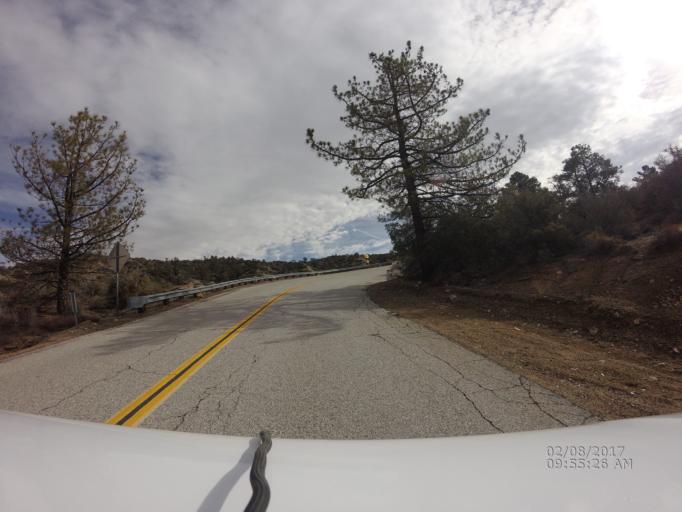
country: US
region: California
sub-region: San Bernardino County
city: Pinon Hills
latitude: 34.4177
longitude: -117.7888
